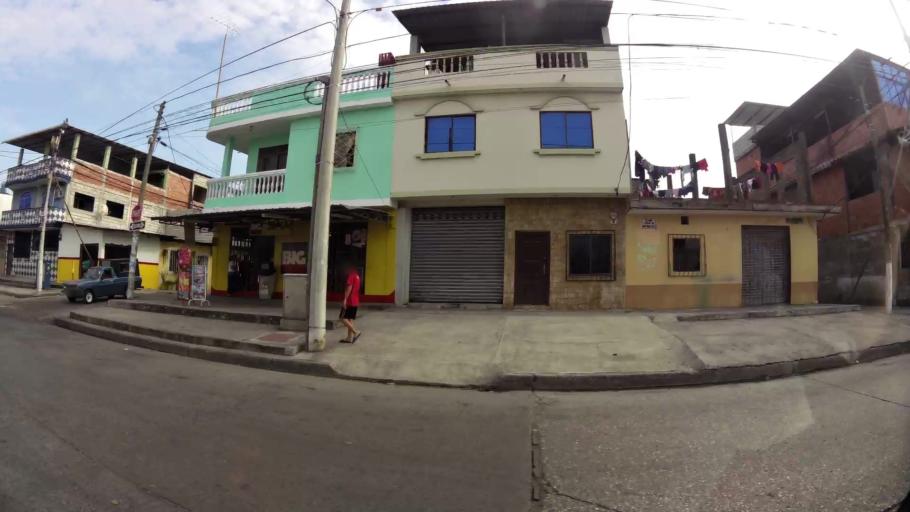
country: EC
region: Guayas
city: Guayaquil
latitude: -2.2437
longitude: -79.8883
